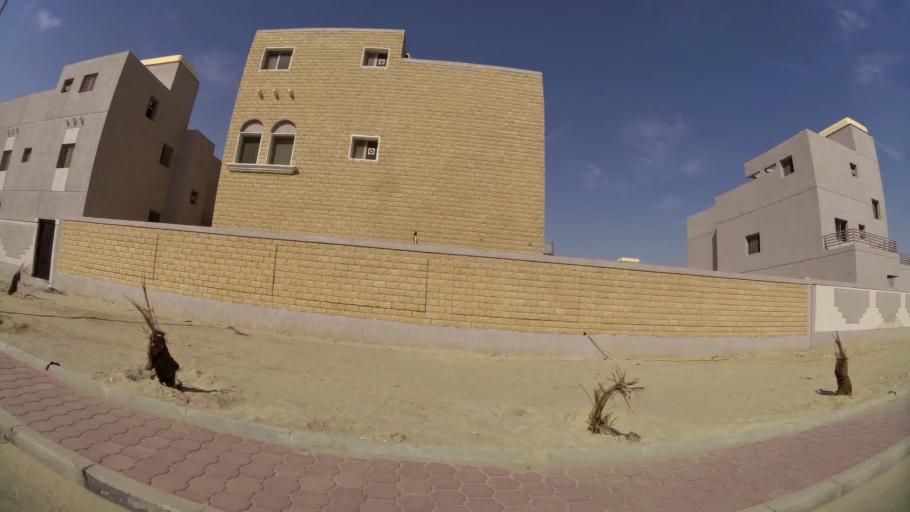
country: KW
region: Al Ahmadi
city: Al Wafrah
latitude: 28.7984
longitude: 48.0754
